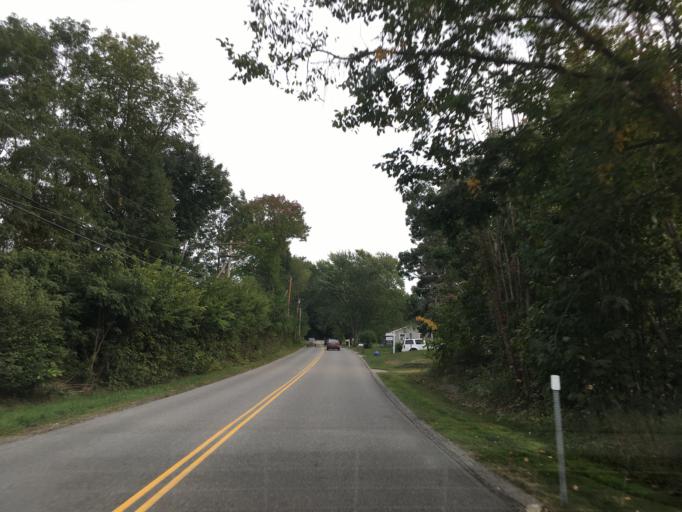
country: US
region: New Hampshire
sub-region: Rockingham County
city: Exeter
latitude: 42.9931
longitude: -70.9223
